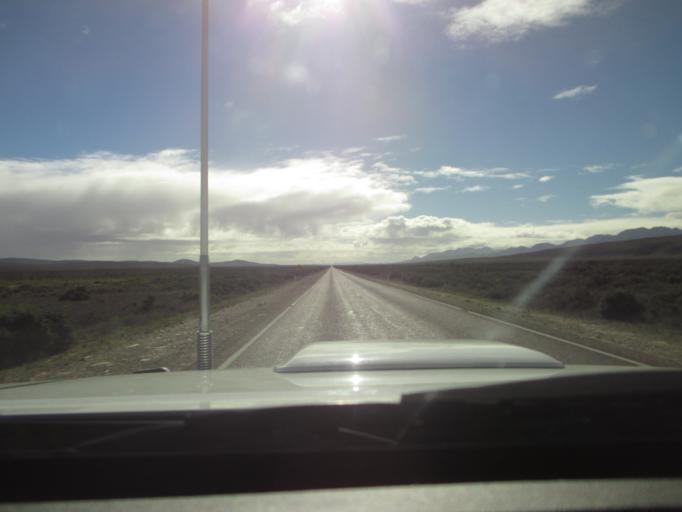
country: AU
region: South Australia
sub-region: Flinders Ranges
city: Quorn
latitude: -31.7329
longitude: 138.3421
